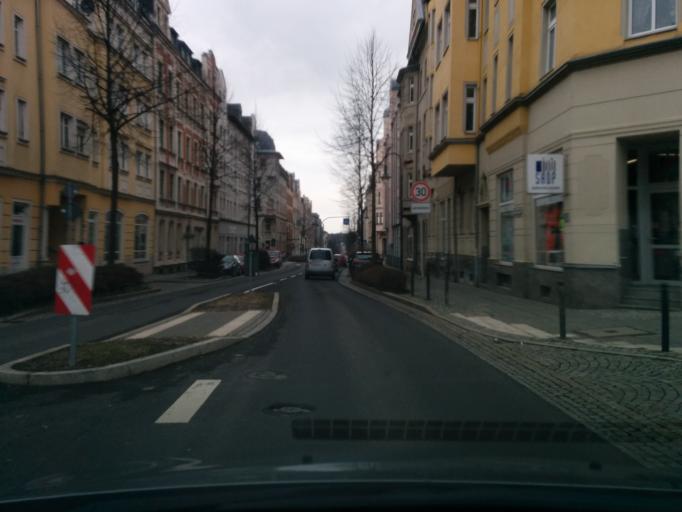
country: DE
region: Saxony
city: Chemnitz
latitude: 50.8365
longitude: 12.9402
